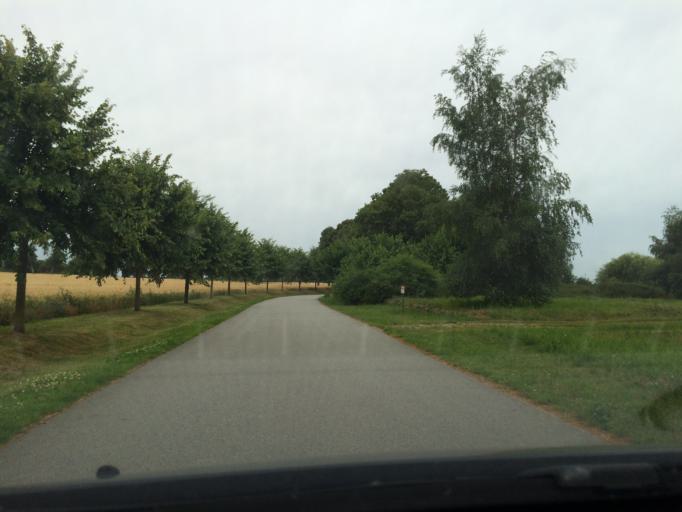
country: DE
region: Mecklenburg-Vorpommern
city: Altenpleen
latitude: 54.4023
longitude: 12.9489
